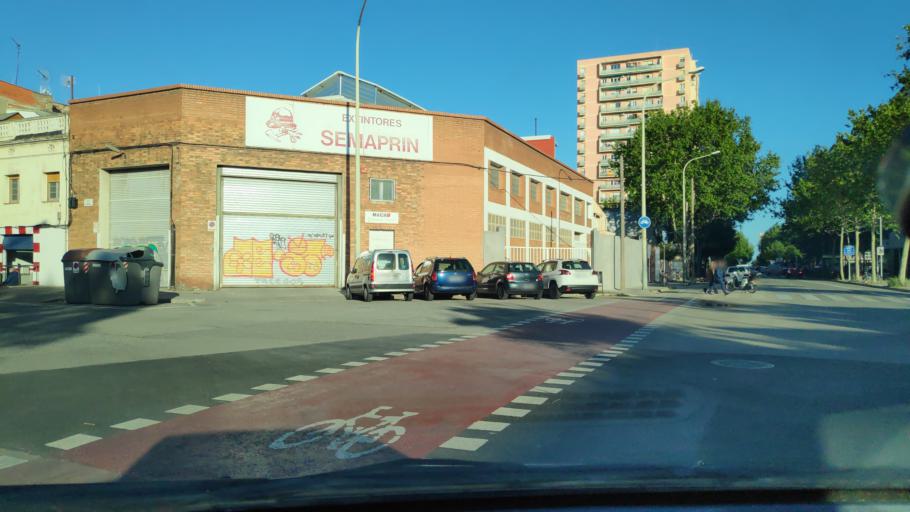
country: ES
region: Catalonia
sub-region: Provincia de Barcelona
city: Sant Marti
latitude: 41.4102
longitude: 2.2073
